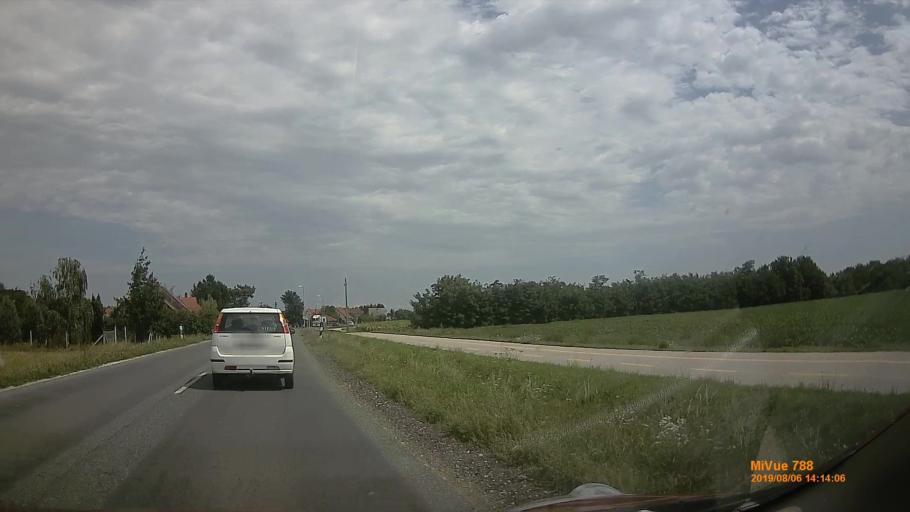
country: HU
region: Vas
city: Taplanszentkereszt
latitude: 47.1978
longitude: 16.6857
